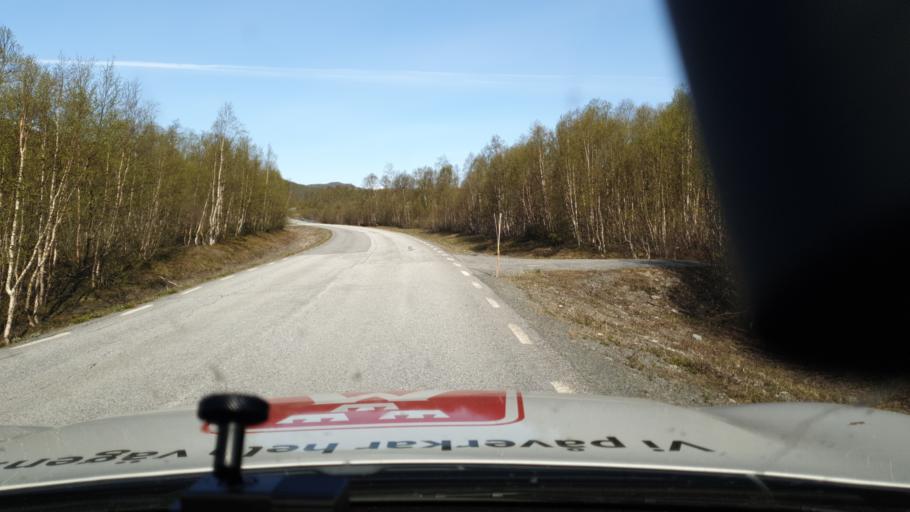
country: NO
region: Nordland
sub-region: Rana
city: Mo i Rana
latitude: 65.7798
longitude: 15.1296
